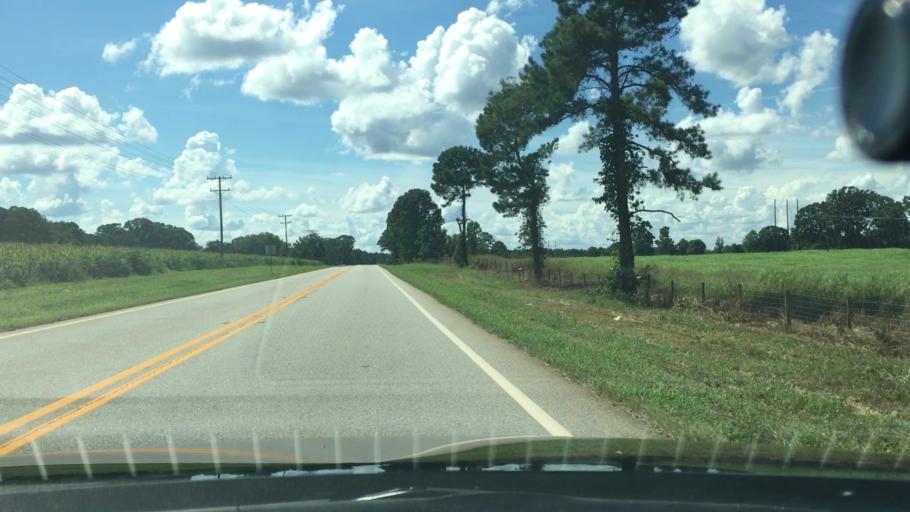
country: US
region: Georgia
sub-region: Jasper County
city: Monticello
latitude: 33.3011
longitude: -83.7249
